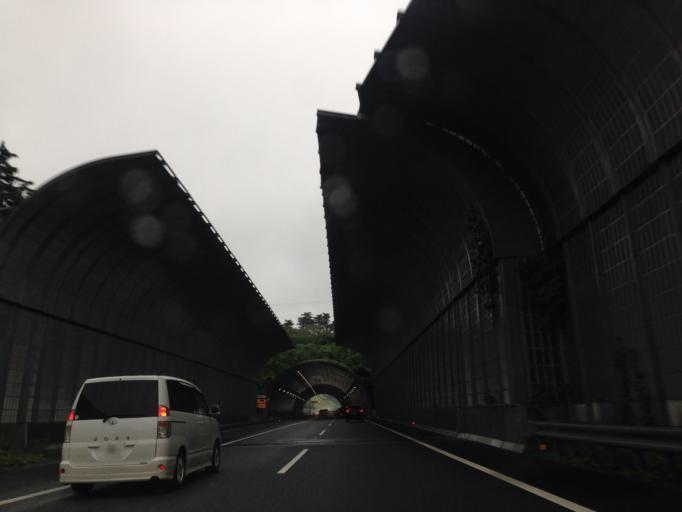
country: JP
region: Shizuoka
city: Mishima
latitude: 35.1983
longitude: 138.8886
